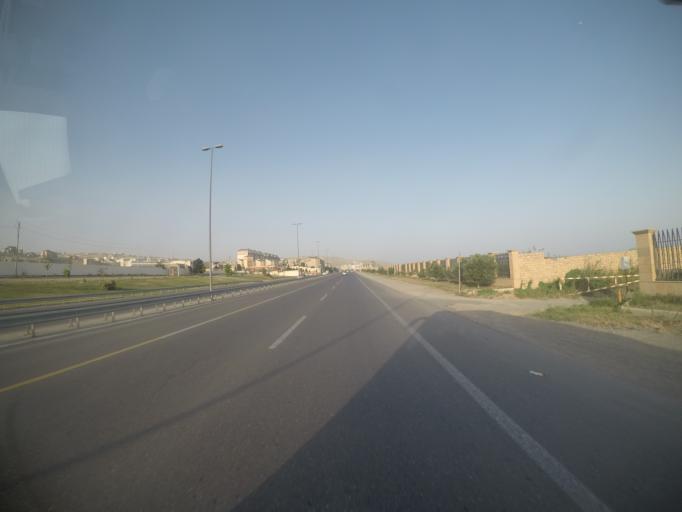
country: AZ
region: Baki
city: Badamdar
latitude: 40.3048
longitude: 49.7829
